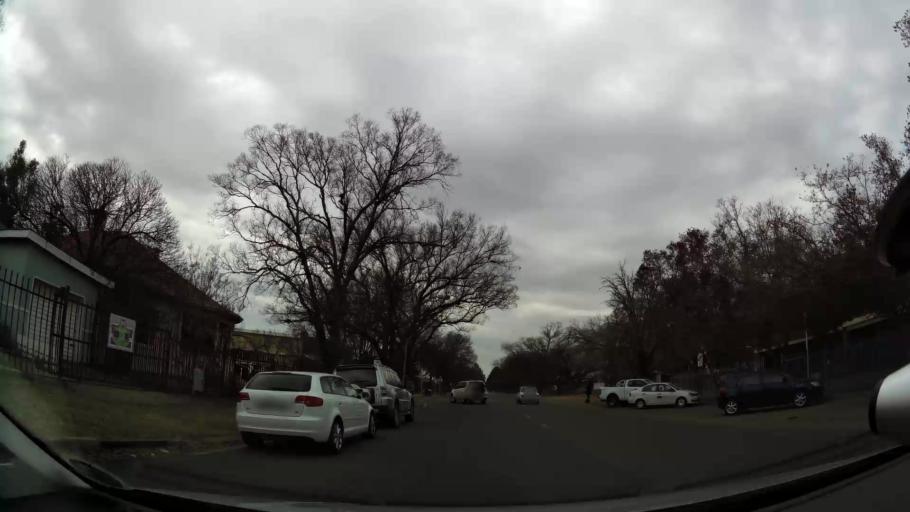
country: ZA
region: Orange Free State
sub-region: Fezile Dabi District Municipality
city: Kroonstad
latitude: -27.6624
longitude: 27.2416
